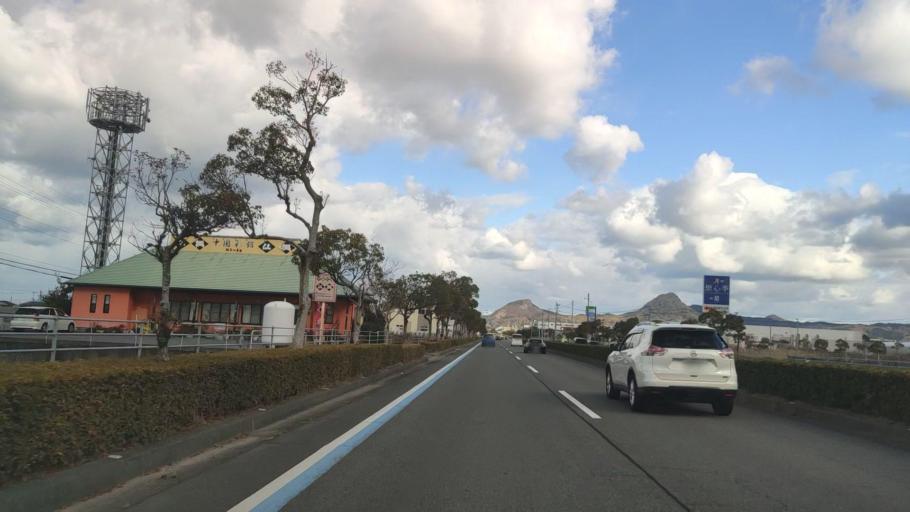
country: JP
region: Ehime
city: Hojo
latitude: 33.9577
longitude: 132.7765
